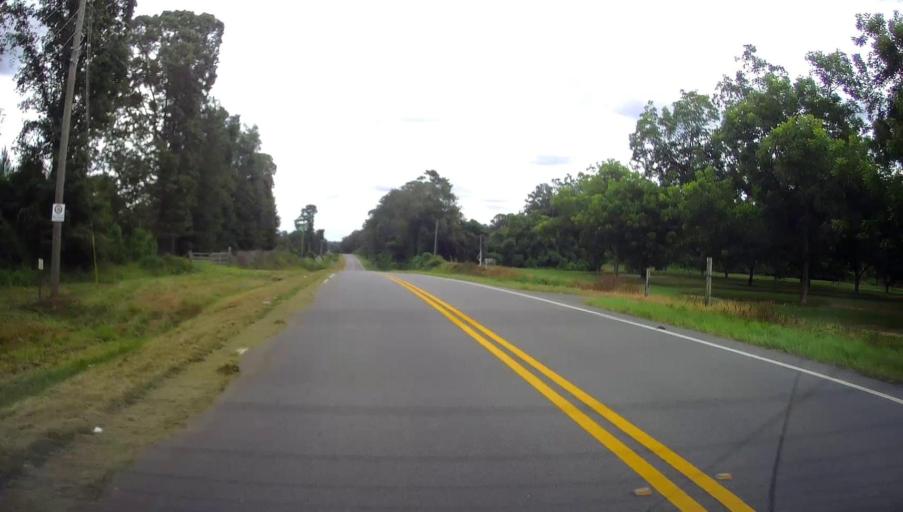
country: US
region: Georgia
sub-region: Macon County
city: Oglethorpe
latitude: 32.2645
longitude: -84.0965
